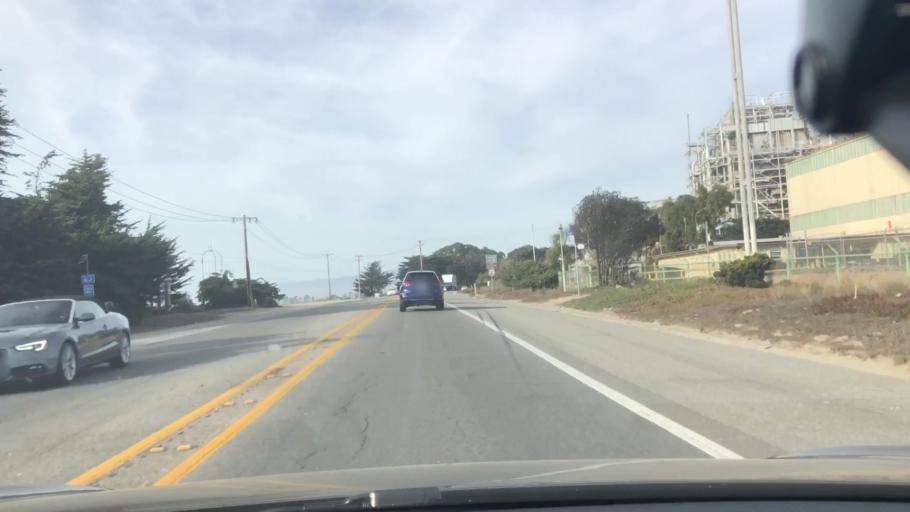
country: US
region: California
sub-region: Monterey County
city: Castroville
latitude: 36.8019
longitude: -121.7836
